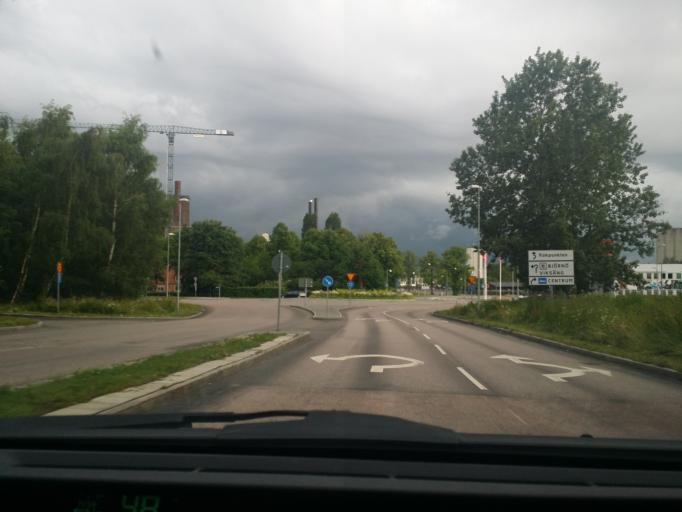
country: SE
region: Vaestmanland
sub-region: Vasteras
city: Vasteras
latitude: 59.6103
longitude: 16.5692
